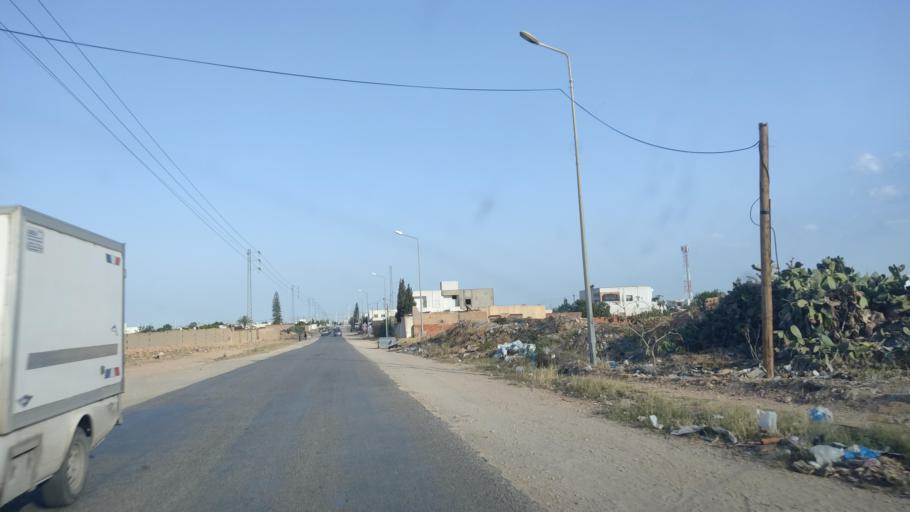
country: TN
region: Safaqis
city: Sfax
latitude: 34.8004
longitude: 10.6740
